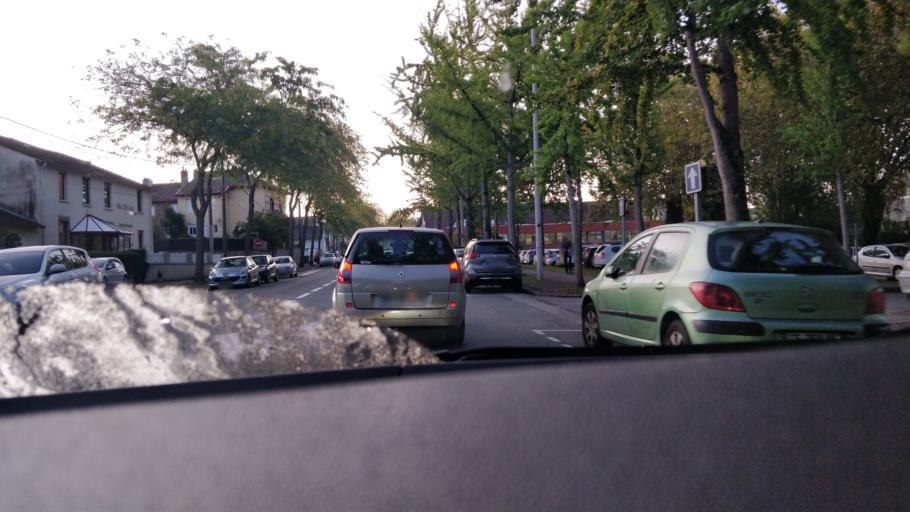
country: FR
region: Limousin
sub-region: Departement de la Haute-Vienne
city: Limoges
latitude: 45.8361
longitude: 1.2430
